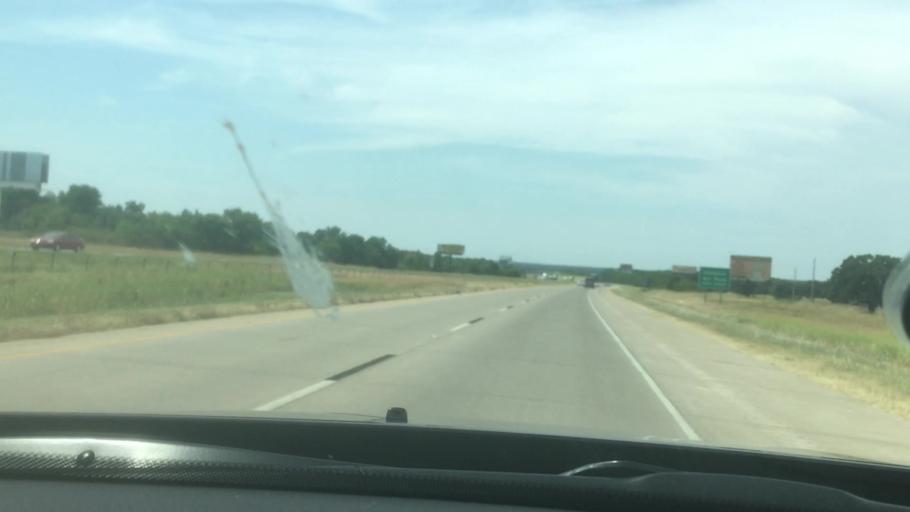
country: US
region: Oklahoma
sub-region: Carter County
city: Ardmore
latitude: 34.3161
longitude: -97.1571
